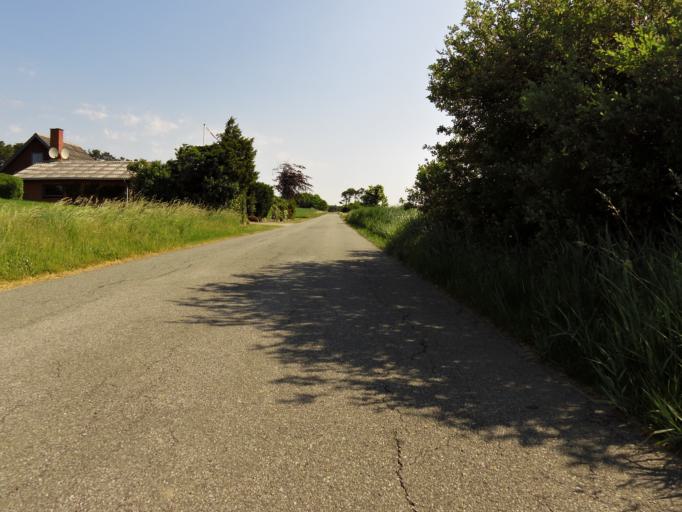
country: DK
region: Central Jutland
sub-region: Holstebro Kommune
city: Vinderup
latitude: 56.5748
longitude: 8.7973
